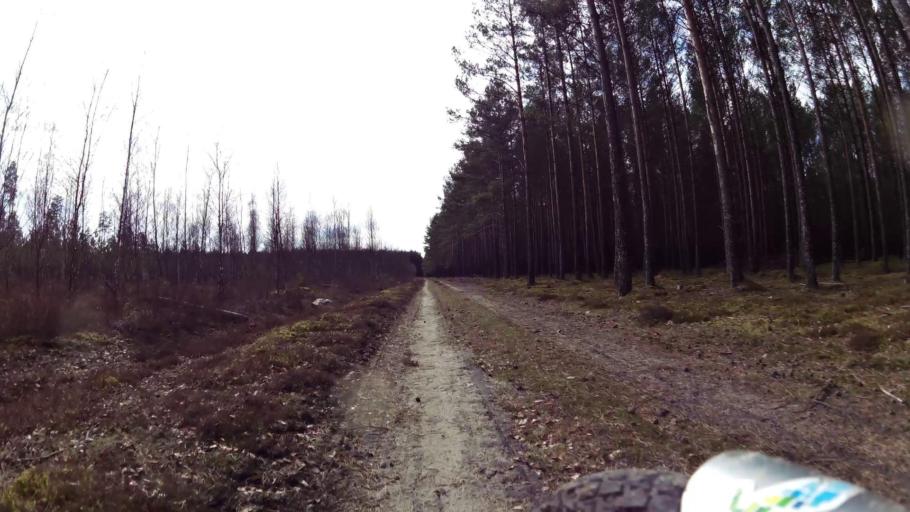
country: PL
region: Pomeranian Voivodeship
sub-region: Powiat bytowski
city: Kolczyglowy
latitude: 54.1904
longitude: 17.2140
